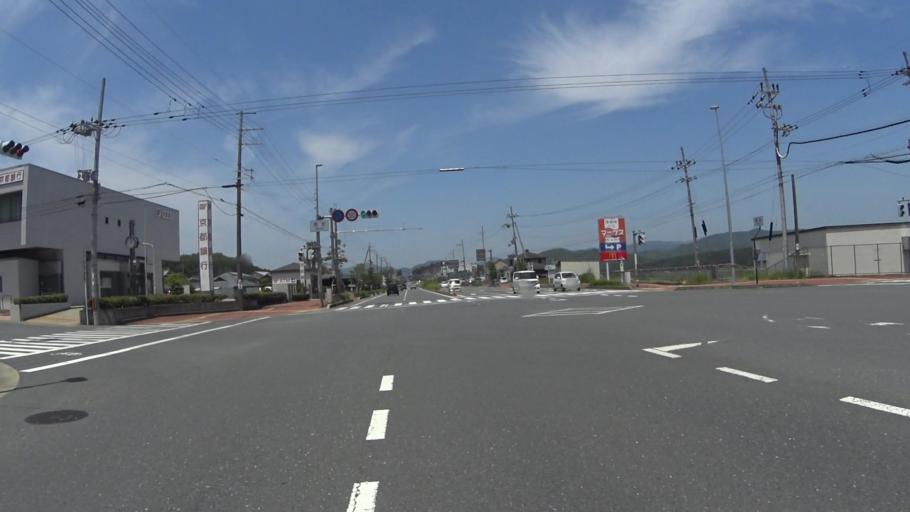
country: JP
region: Kyoto
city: Kameoka
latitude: 35.1558
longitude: 135.4267
